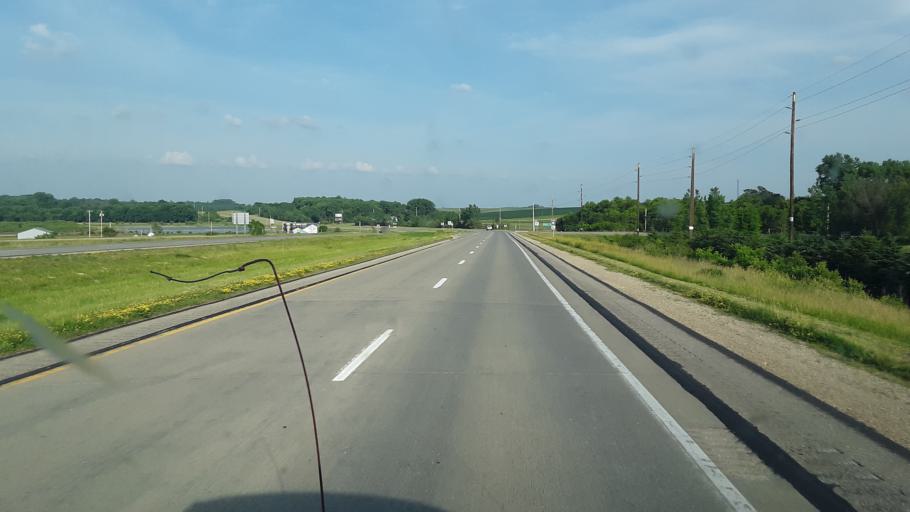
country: US
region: Iowa
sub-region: Marshall County
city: Marshalltown
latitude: 42.0085
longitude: -92.7699
